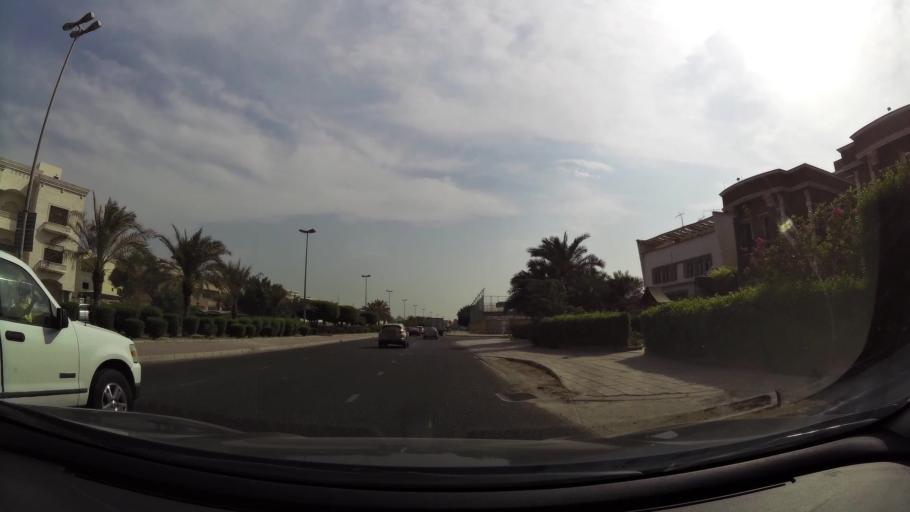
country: KW
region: Al Asimah
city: Ash Shamiyah
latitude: 29.3226
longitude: 47.9642
